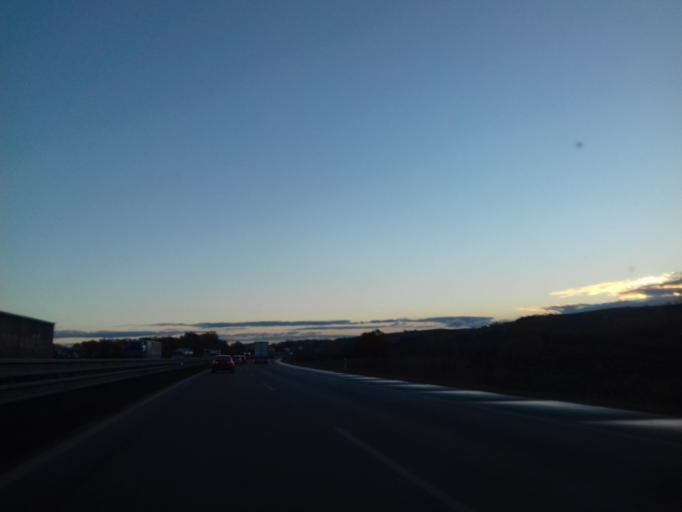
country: CZ
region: South Moravian
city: Rousinov
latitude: 49.1886
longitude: 16.8521
